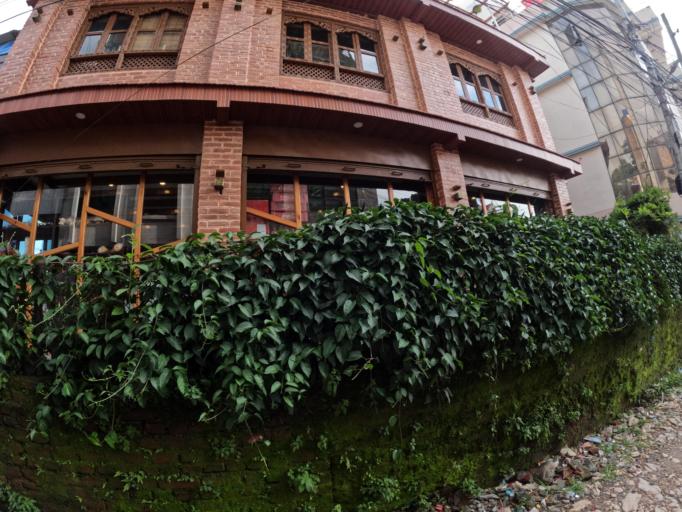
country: NP
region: Central Region
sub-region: Bagmati Zone
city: Kathmandu
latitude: 27.7687
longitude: 85.3305
